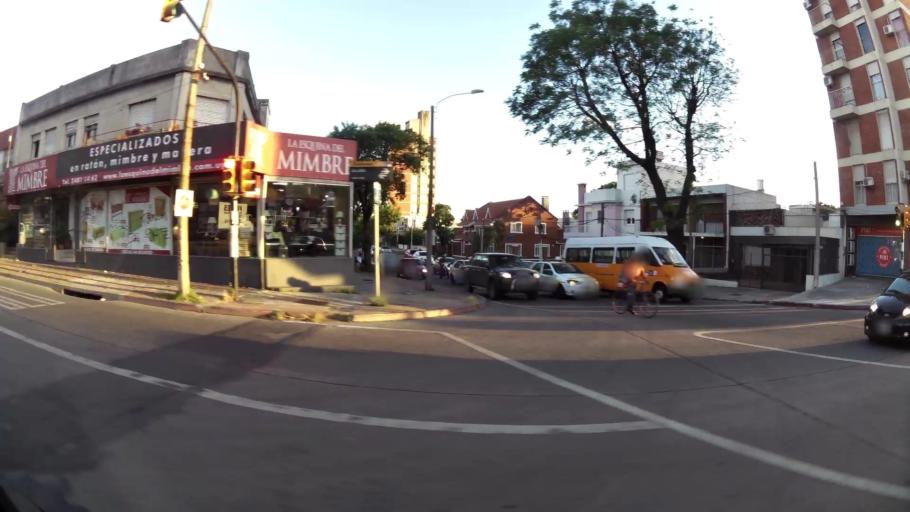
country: UY
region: Montevideo
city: Montevideo
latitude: -34.8877
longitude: -56.1443
